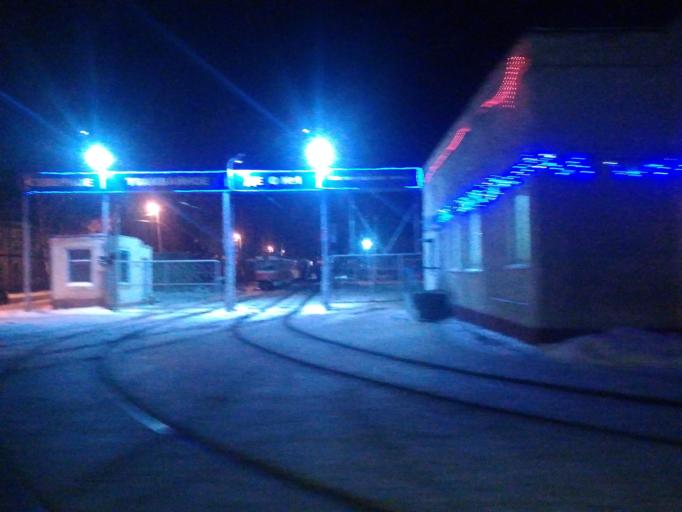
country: RU
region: Ulyanovsk
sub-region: Ulyanovskiy Rayon
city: Ulyanovsk
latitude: 54.3419
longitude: 48.3951
